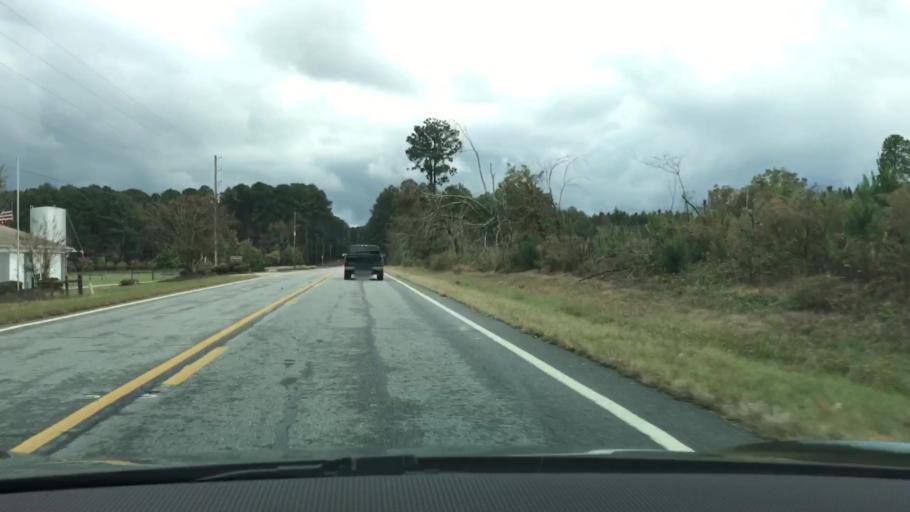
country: US
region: Georgia
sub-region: Oconee County
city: Watkinsville
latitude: 33.7868
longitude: -83.3172
